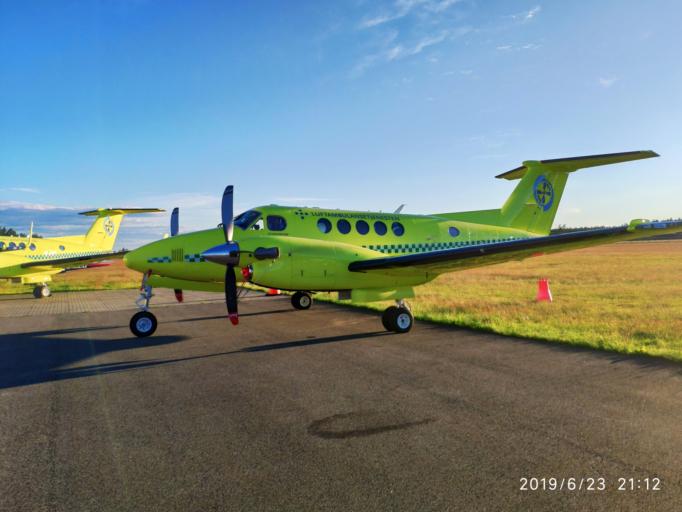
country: NO
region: Buskerud
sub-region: Ringerike
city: Honefoss
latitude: 60.2107
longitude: 10.3160
